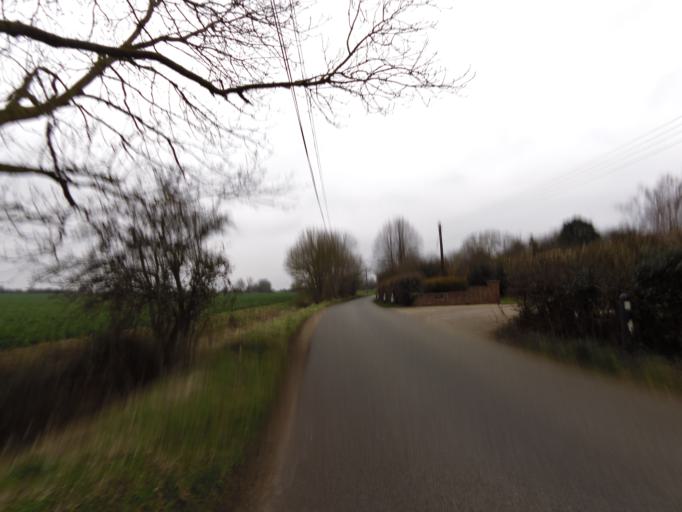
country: GB
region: England
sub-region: Suffolk
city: Framlingham
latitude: 52.2204
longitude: 1.3336
